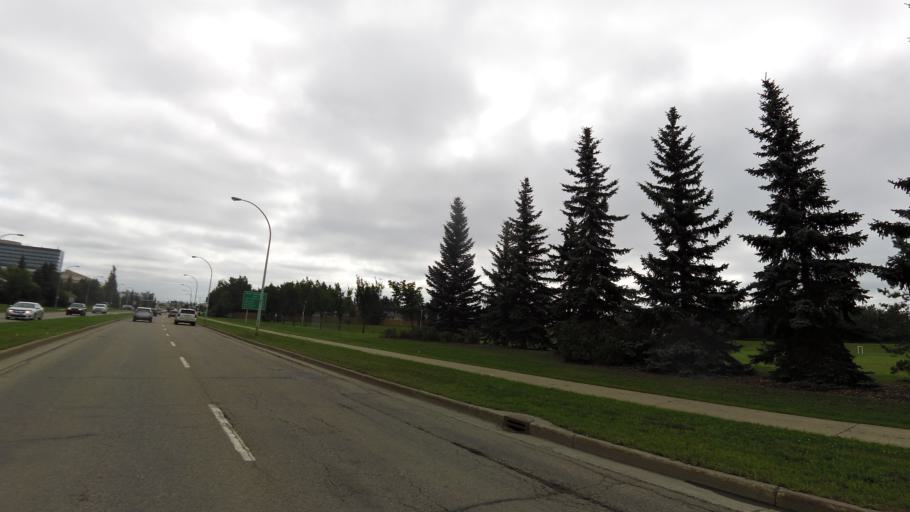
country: CA
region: Alberta
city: St. Albert
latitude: 53.5215
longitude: -113.6356
